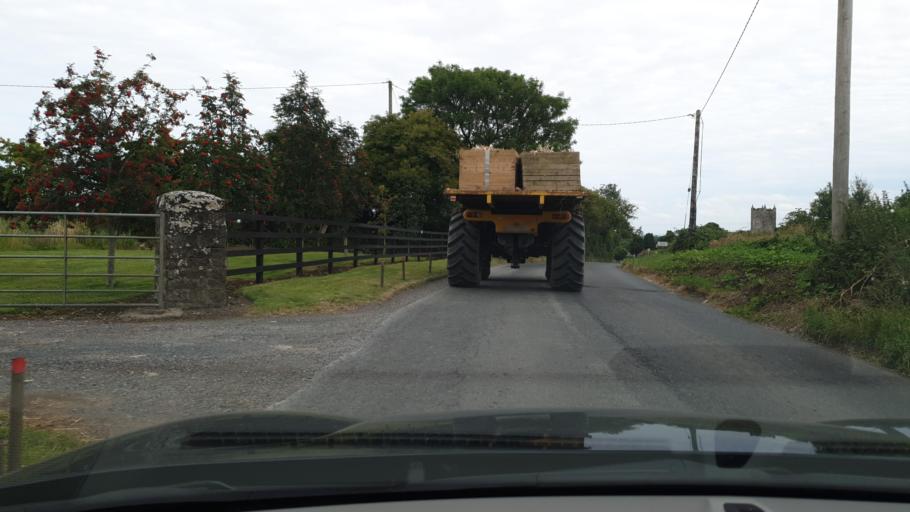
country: IE
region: Leinster
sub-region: An Mhi
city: Ashbourne
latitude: 53.5695
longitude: -6.3870
